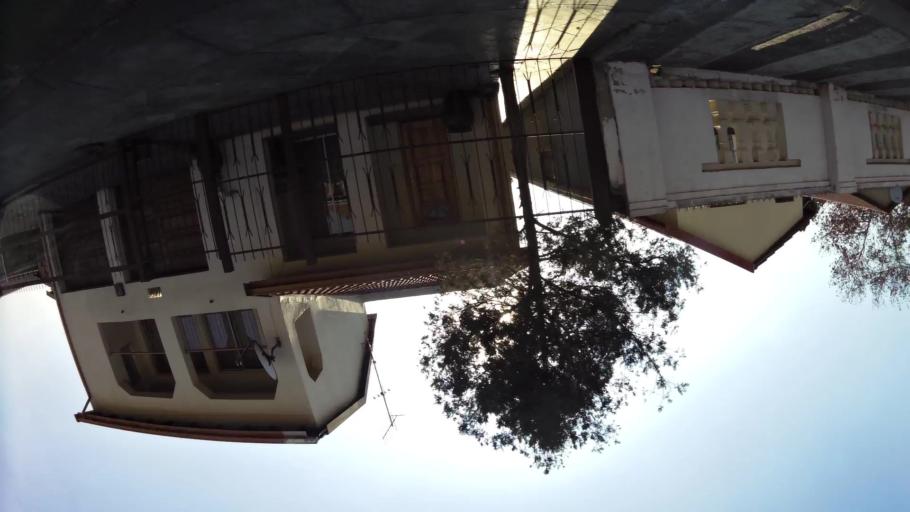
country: ZA
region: North-West
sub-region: Bojanala Platinum District Municipality
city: Rustenburg
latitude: -25.6507
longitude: 27.2205
